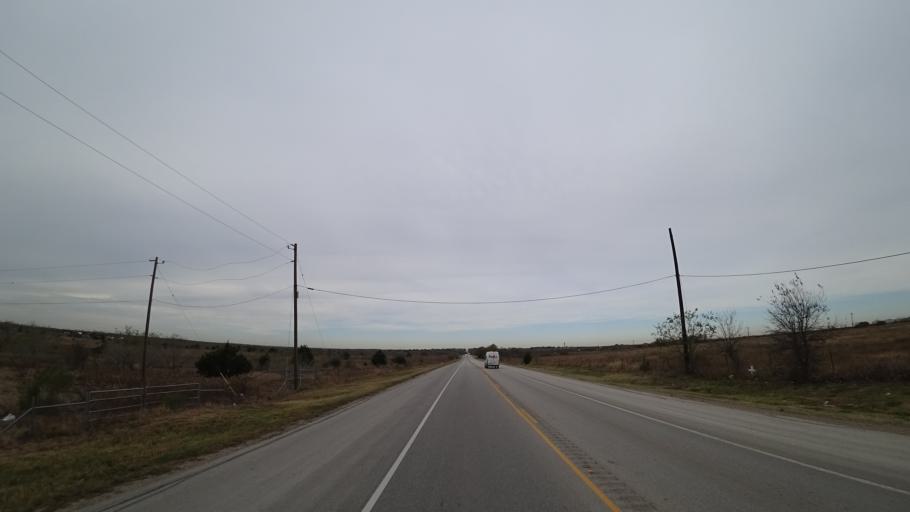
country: US
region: Texas
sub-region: Travis County
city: Garfield
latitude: 30.1072
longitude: -97.6194
